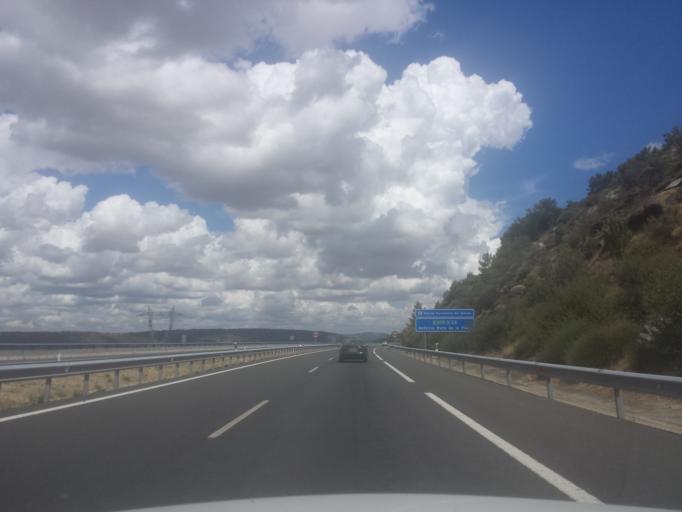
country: ES
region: Castille and Leon
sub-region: Provincia de Salamanca
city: Puerto de Bejar
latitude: 40.3534
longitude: -5.8418
